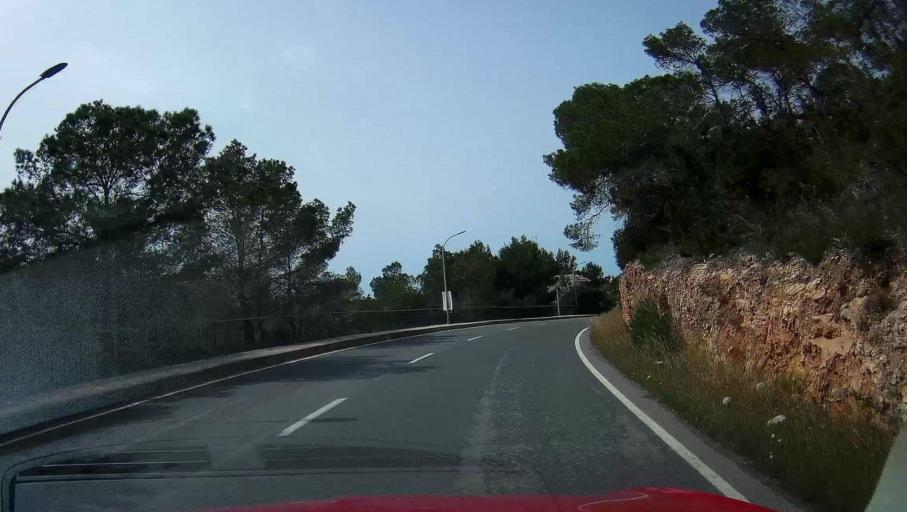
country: ES
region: Balearic Islands
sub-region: Illes Balears
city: Sant Joan de Labritja
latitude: 39.1079
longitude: 1.5204
